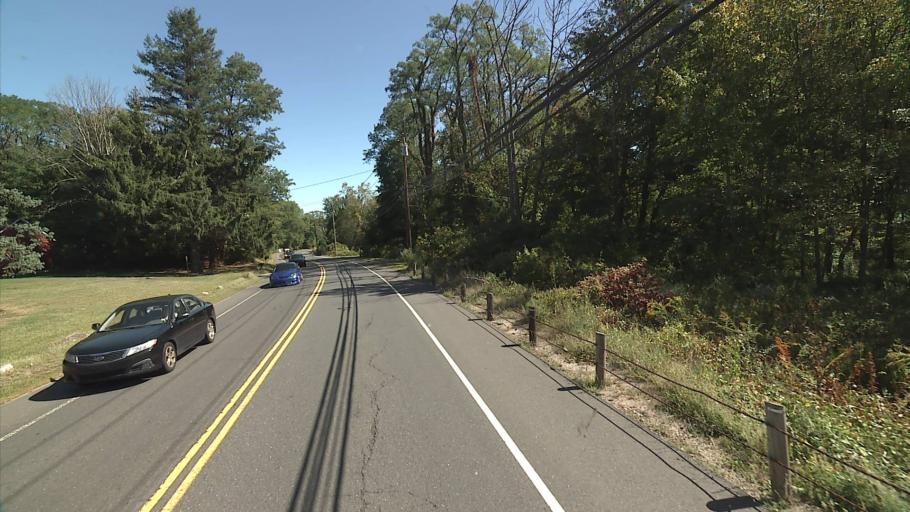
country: US
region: Connecticut
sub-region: New Haven County
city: Prospect
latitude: 41.4987
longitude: -72.9588
